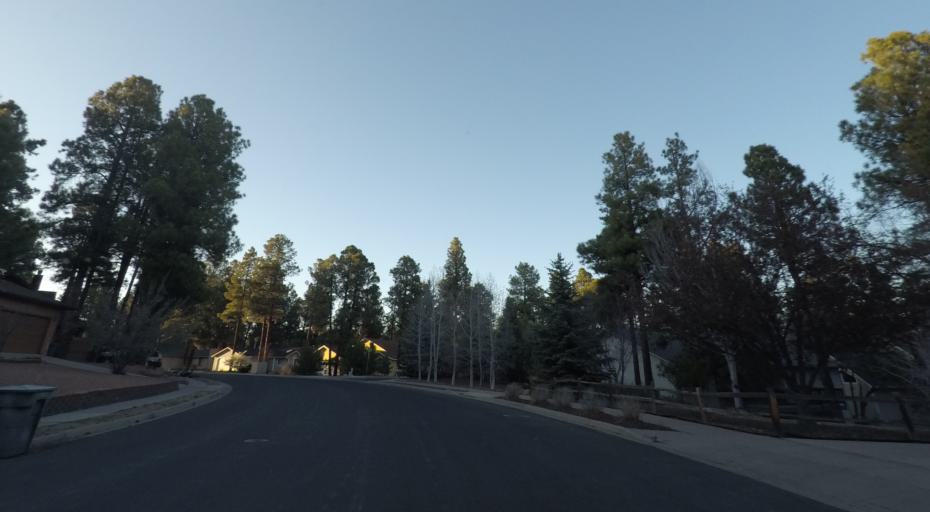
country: US
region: Arizona
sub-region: Coconino County
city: Flagstaff
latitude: 35.1760
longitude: -111.6790
